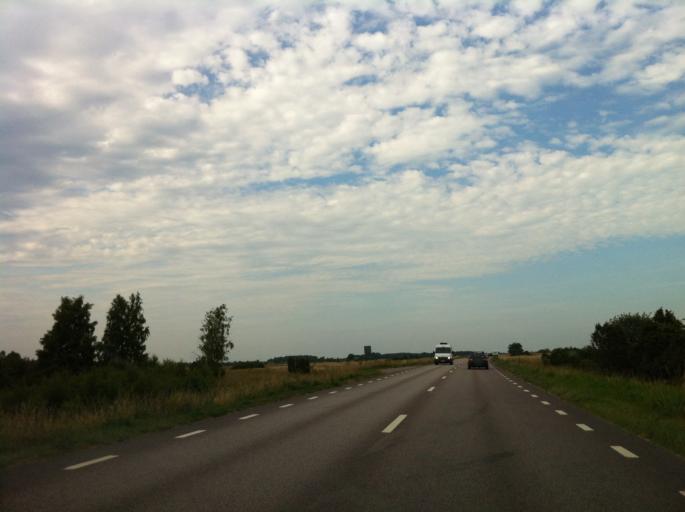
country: SE
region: Kalmar
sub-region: Borgholms Kommun
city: Borgholm
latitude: 56.9740
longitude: 16.8048
